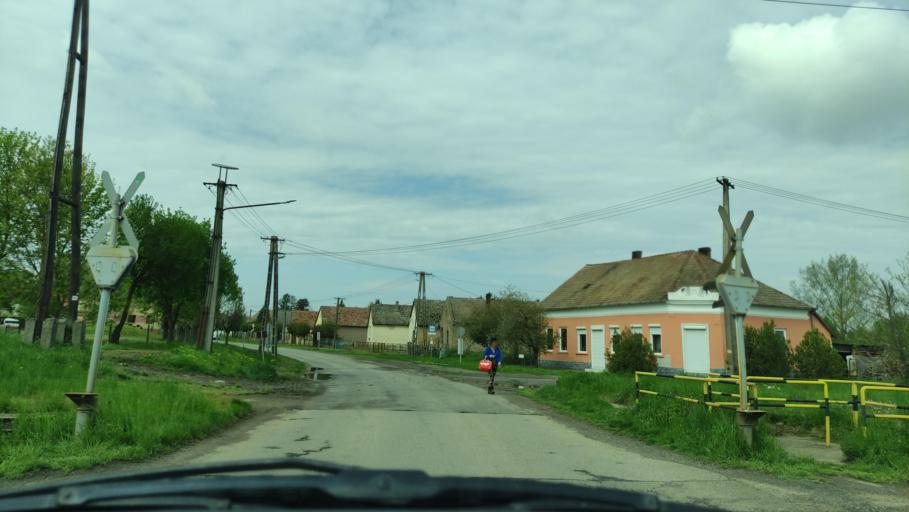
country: HU
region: Baranya
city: Sasd
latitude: 46.3073
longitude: 18.1383
